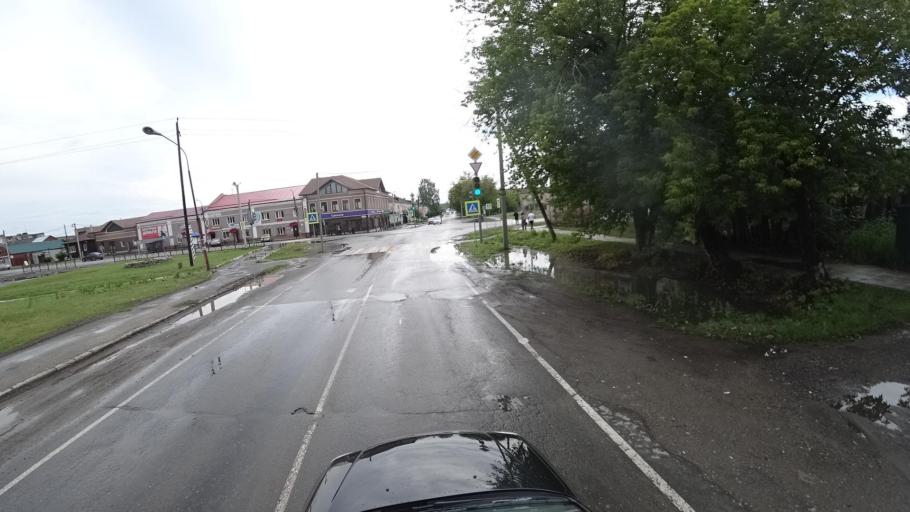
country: RU
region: Sverdlovsk
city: Kamyshlov
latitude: 56.8470
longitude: 62.7125
